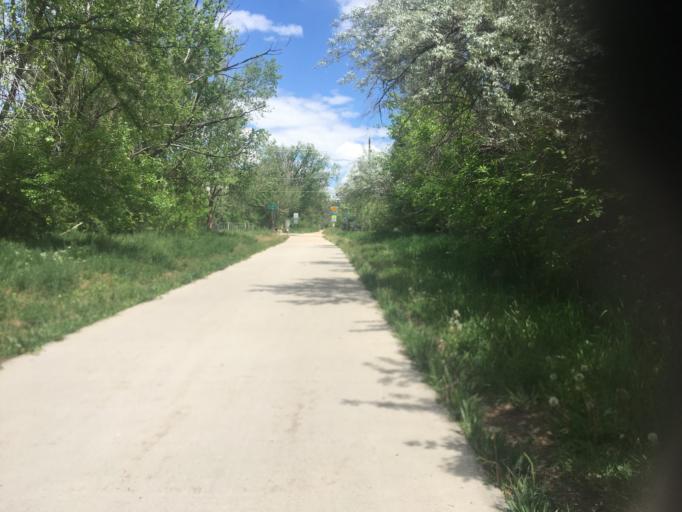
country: US
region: Colorado
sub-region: Boulder County
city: Boulder
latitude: 40.0071
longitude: -105.2356
